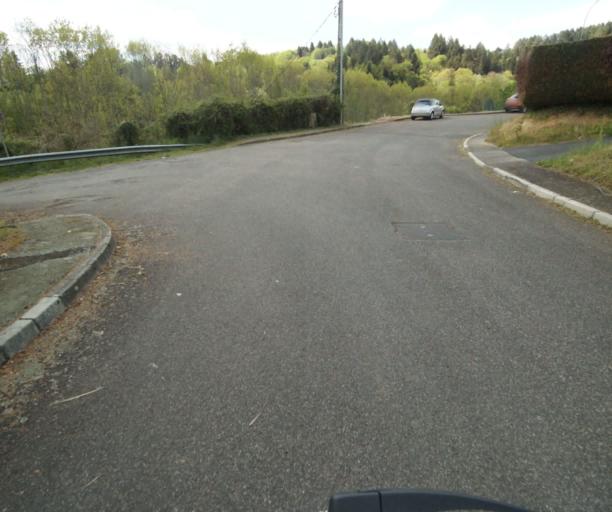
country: FR
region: Limousin
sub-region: Departement de la Correze
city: Tulle
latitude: 45.2775
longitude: 1.7626
